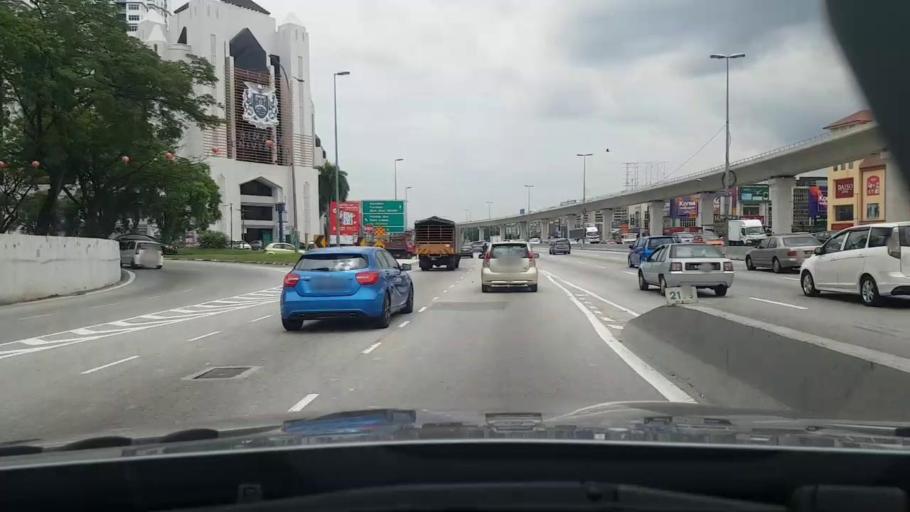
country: MY
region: Selangor
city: Subang Jaya
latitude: 3.0445
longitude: 101.6196
